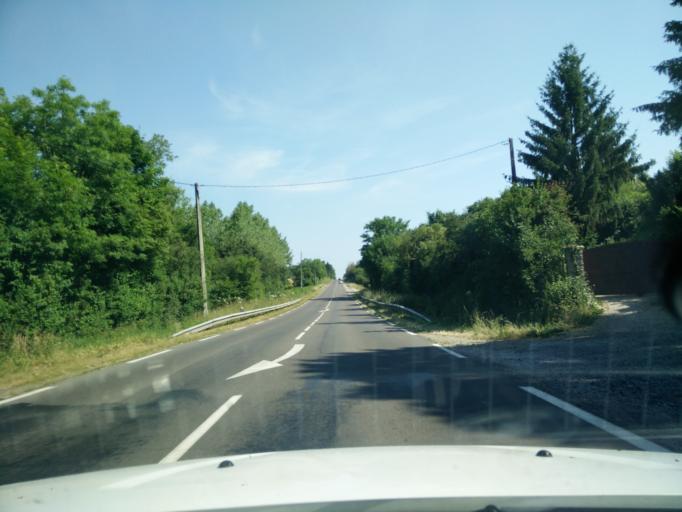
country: FR
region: Auvergne
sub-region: Departement de l'Allier
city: Toulon-sur-Allier
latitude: 46.5209
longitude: 3.3180
